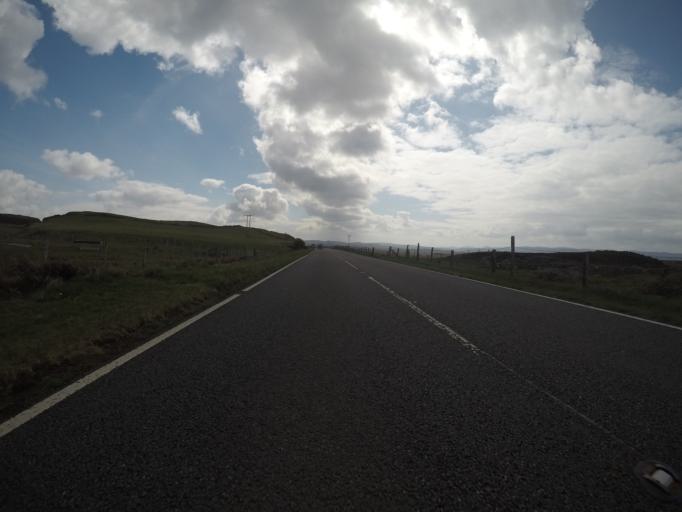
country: GB
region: Scotland
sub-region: Highland
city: Portree
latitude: 57.5543
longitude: -6.3655
